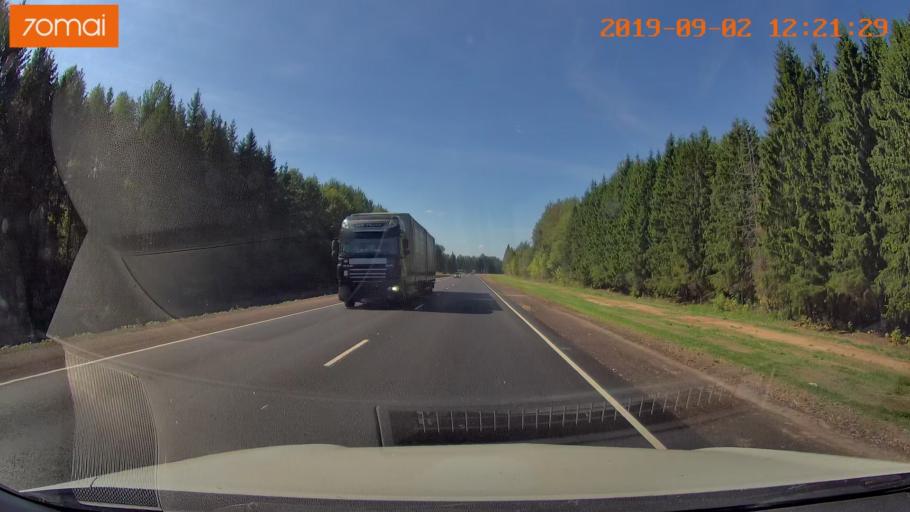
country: RU
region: Smolensk
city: Oster
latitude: 53.8874
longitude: 32.6549
